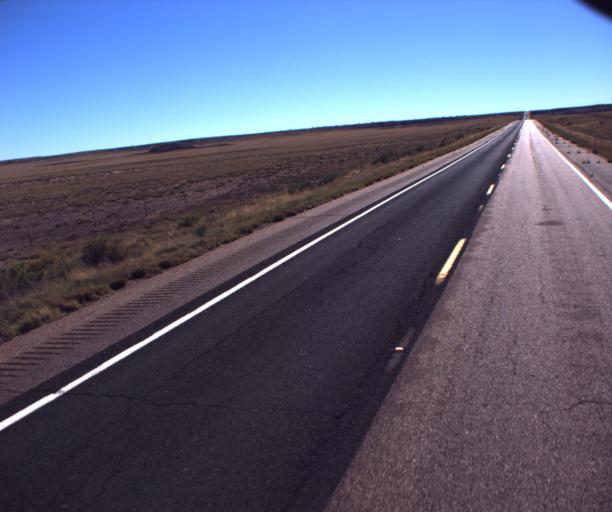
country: US
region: Arizona
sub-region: Navajo County
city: Snowflake
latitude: 34.7312
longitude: -109.7829
